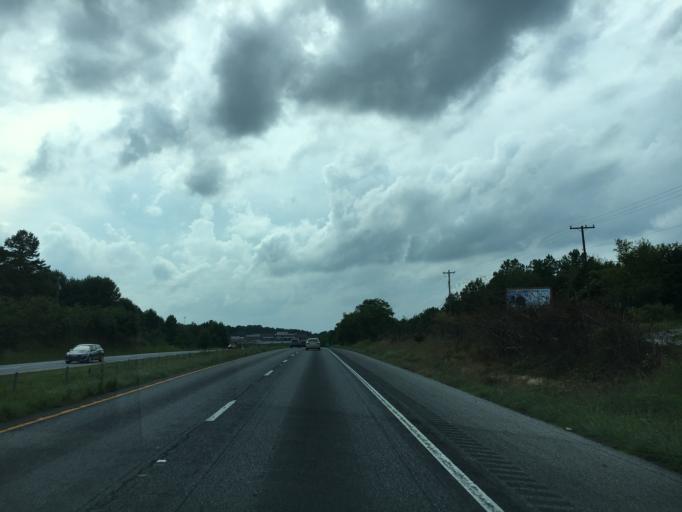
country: US
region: South Carolina
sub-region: Spartanburg County
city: Cowpens
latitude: 35.0736
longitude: -81.7530
